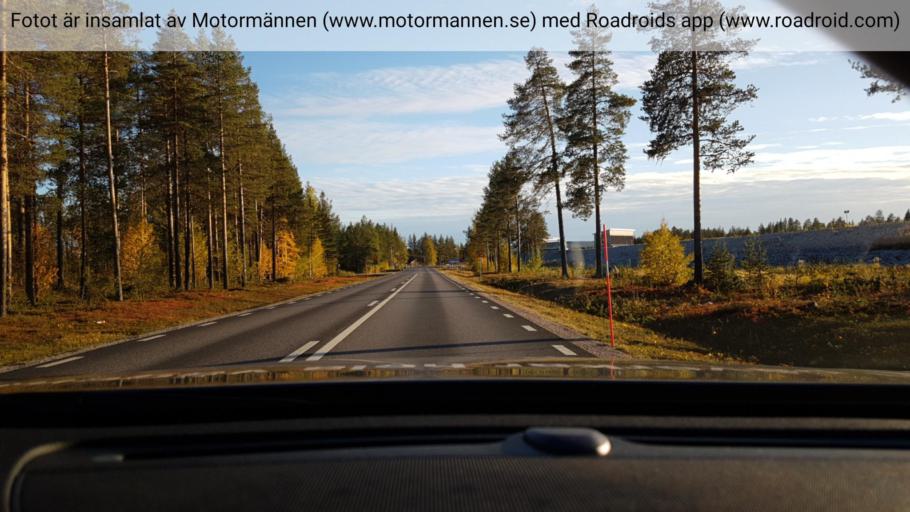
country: SE
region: Norrbotten
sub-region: Jokkmokks Kommun
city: Jokkmokk
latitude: 66.6342
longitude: 19.8233
